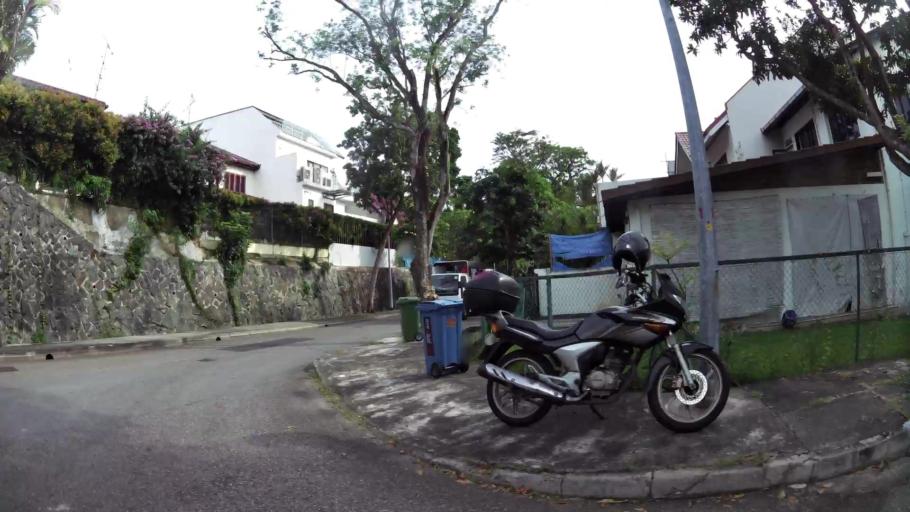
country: SG
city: Singapore
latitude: 1.3271
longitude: 103.8186
